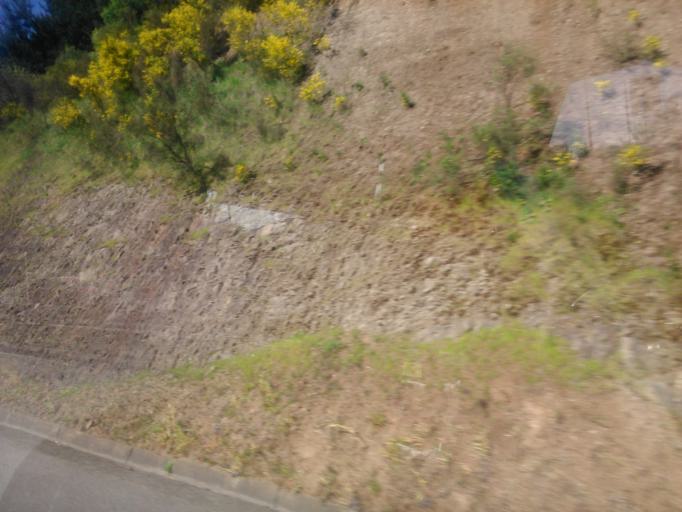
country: CL
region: Araucania
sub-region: Provincia de Cautin
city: Temuco
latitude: -38.8053
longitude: -72.6269
